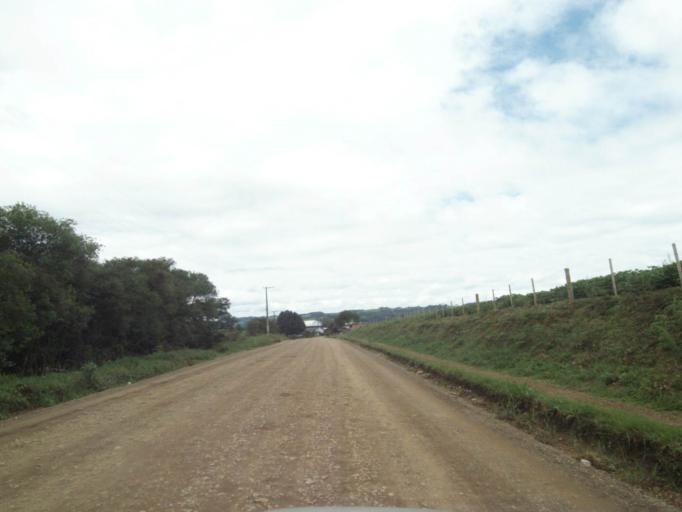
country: BR
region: Rio Grande do Sul
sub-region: Lagoa Vermelha
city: Lagoa Vermelha
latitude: -28.2220
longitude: -51.5381
